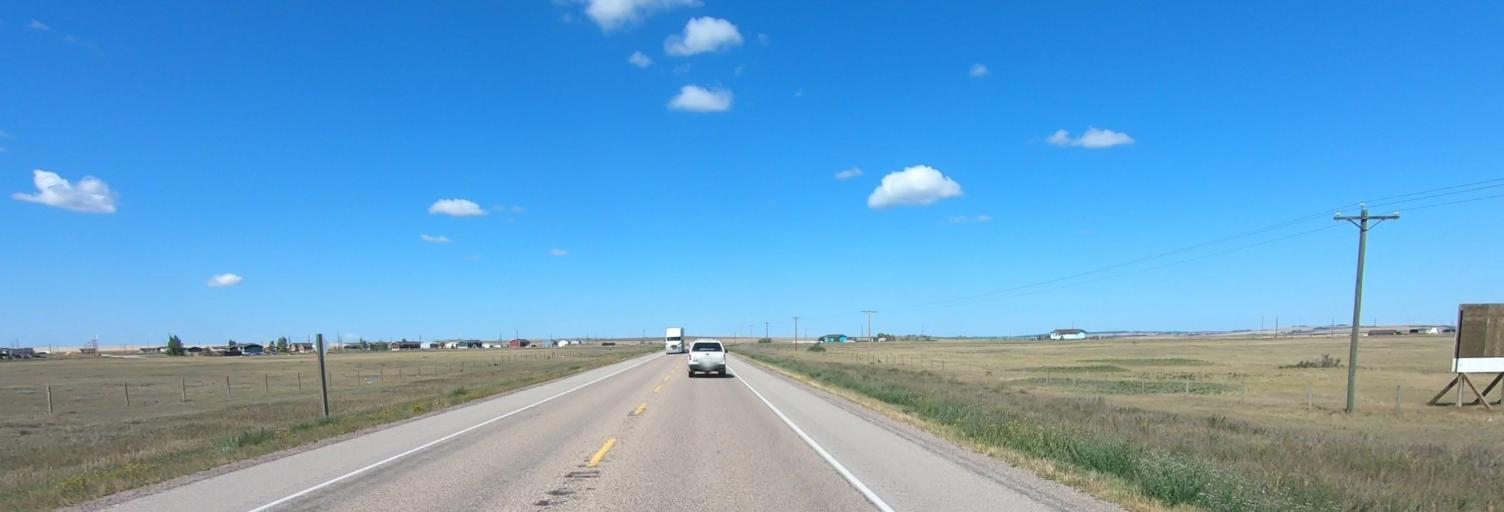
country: CA
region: Alberta
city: Strathmore
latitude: 50.8860
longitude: -113.1844
